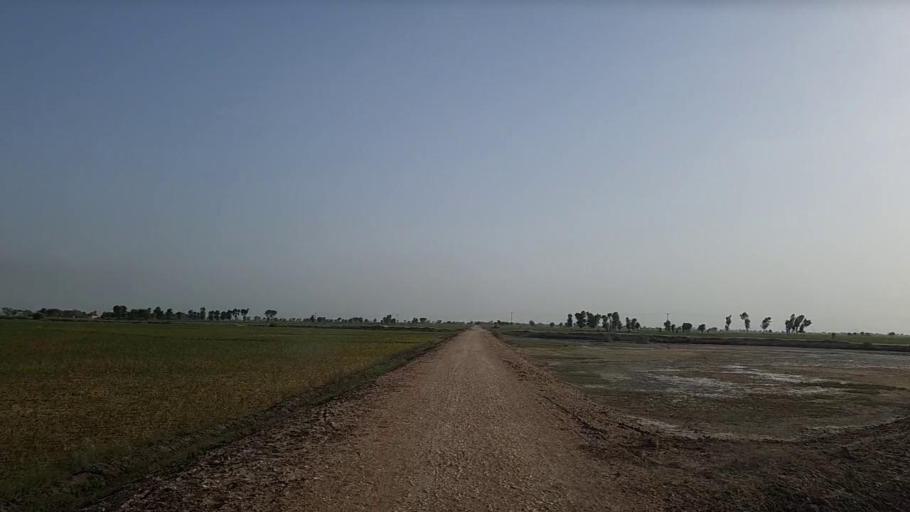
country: PK
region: Sindh
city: Sita Road
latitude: 27.1027
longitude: 67.8872
